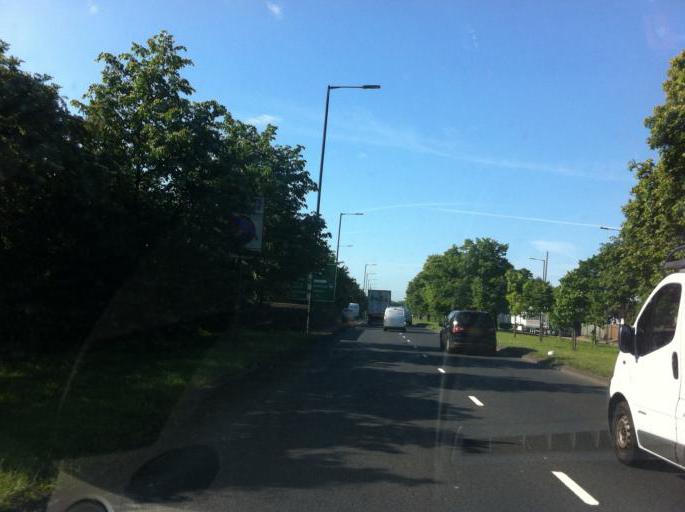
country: GB
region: England
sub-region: Greater London
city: Feltham
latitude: 51.4760
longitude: -0.4046
